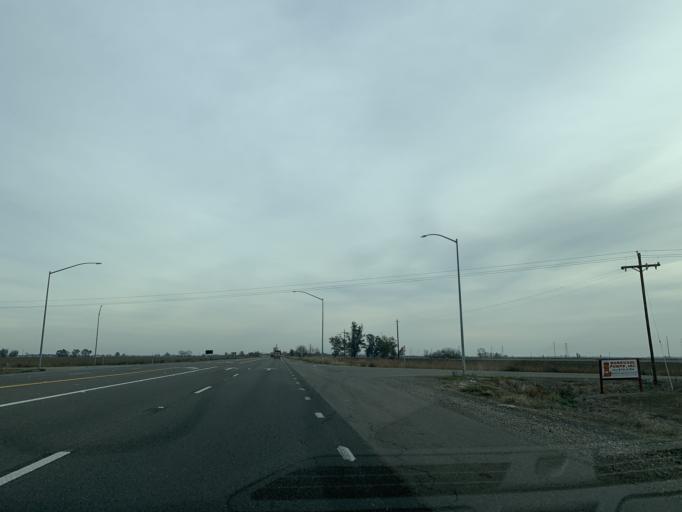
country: US
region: California
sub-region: Yuba County
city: Plumas Lake
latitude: 38.8670
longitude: -121.5554
